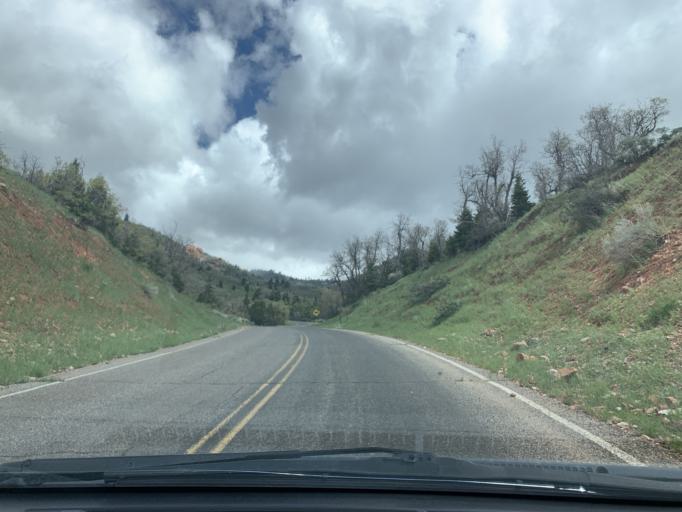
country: US
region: Utah
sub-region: Sanpete County
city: Fountain Green
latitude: 39.7840
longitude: -111.6902
